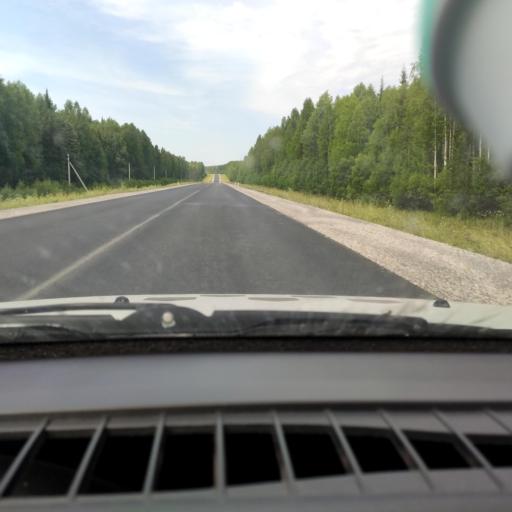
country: RU
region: Perm
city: Siva
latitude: 58.5824
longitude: 53.8837
